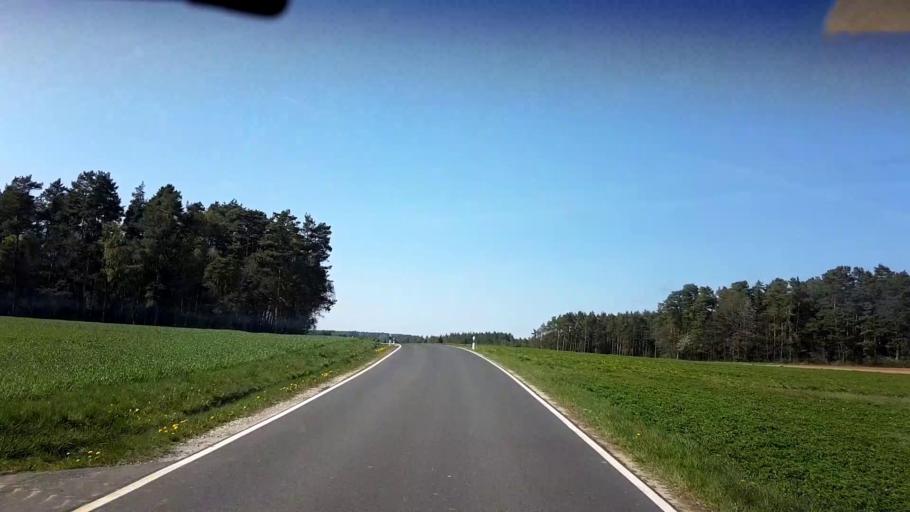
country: DE
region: Bavaria
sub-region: Upper Franconia
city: Pottenstein
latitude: 49.8023
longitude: 11.3737
